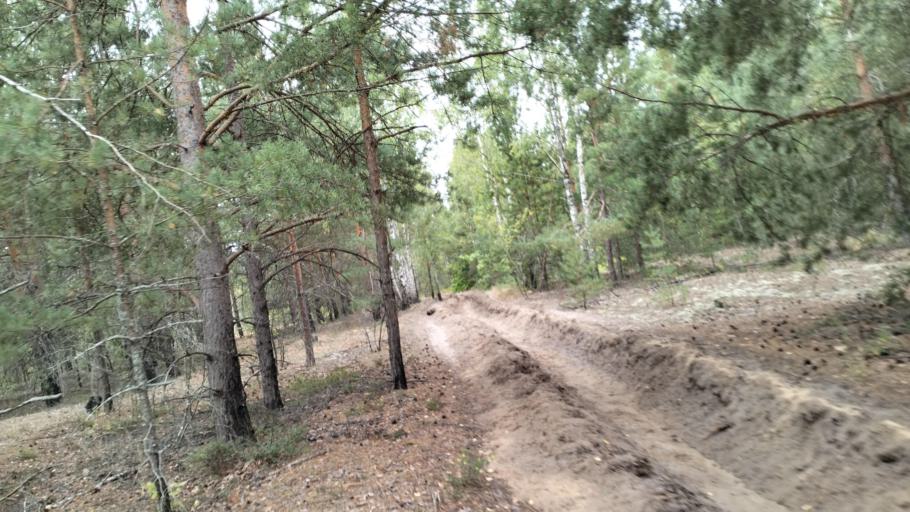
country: BY
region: Brest
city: Davyd-Haradok
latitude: 51.8761
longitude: 27.2106
